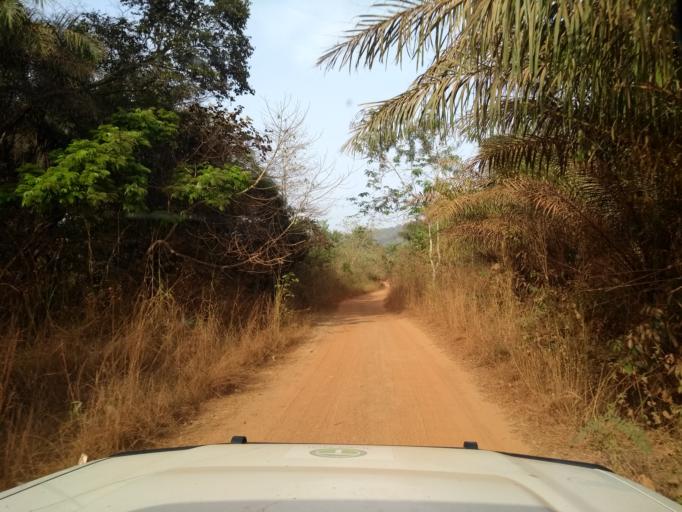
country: GN
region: Kindia
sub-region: Prefecture de Dubreka
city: Dubreka
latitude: 9.8460
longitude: -13.5601
